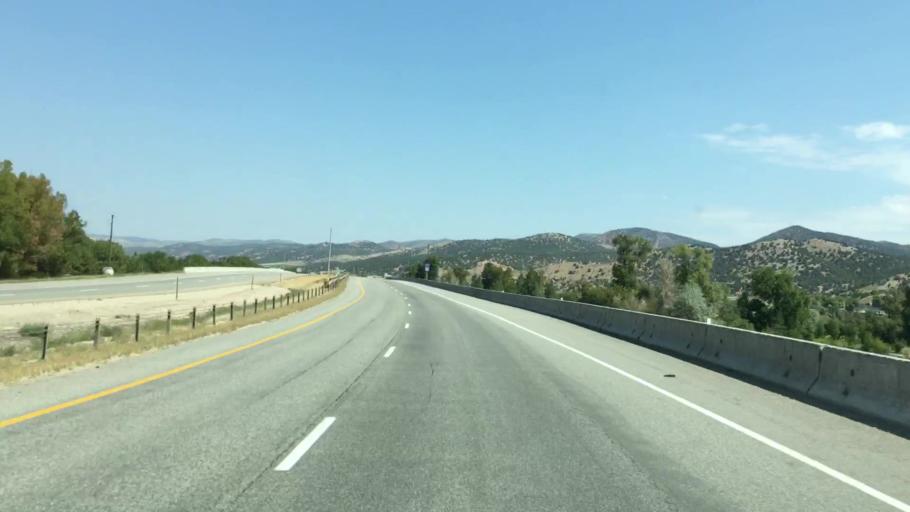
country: US
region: Utah
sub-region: Summit County
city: Coalville
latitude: 40.8110
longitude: -111.4026
